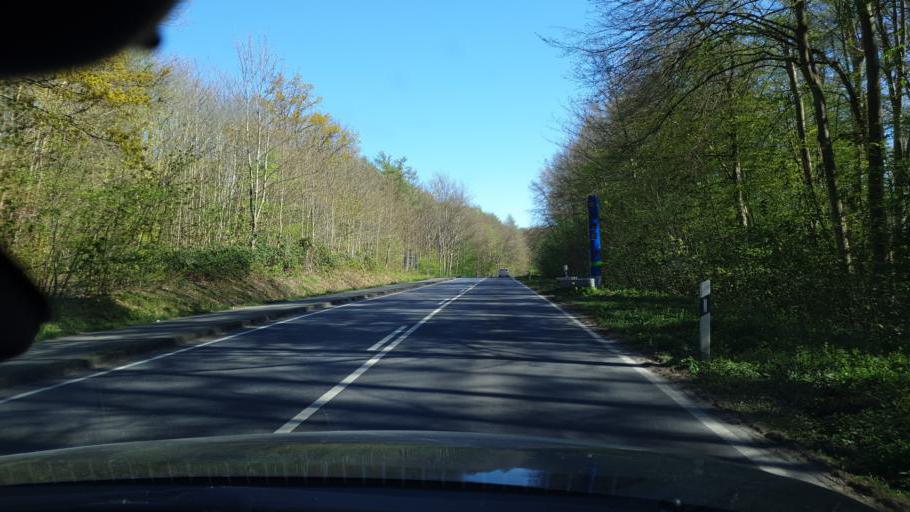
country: DE
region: Mecklenburg-Vorpommern
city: Werdervorstadt
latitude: 53.6512
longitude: 11.4320
